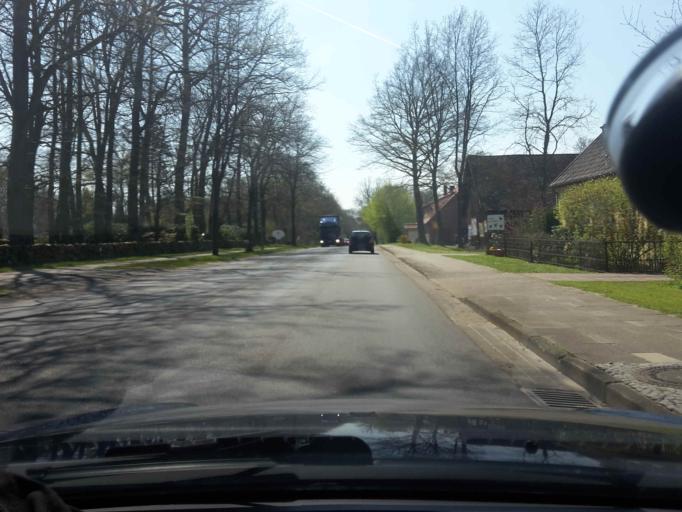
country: DE
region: Lower Saxony
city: Schneverdingen
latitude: 53.0728
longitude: 9.8632
